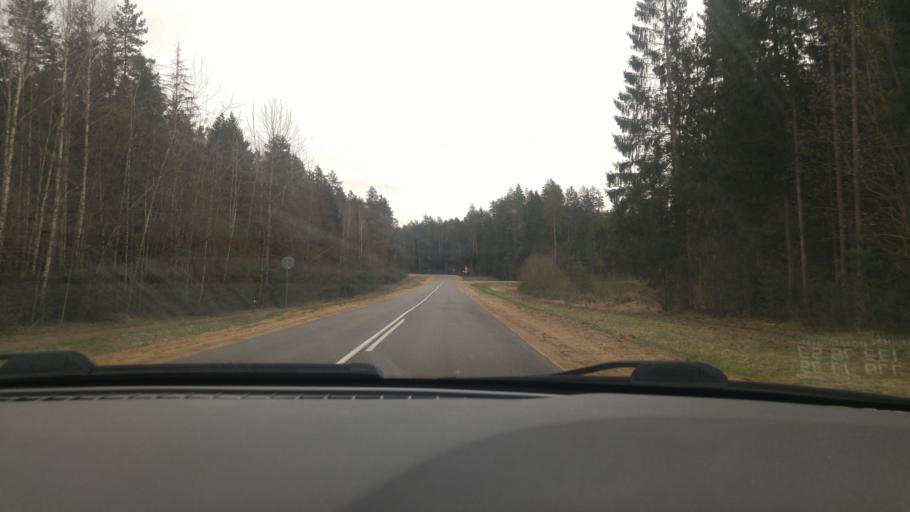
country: BY
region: Minsk
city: Chervyen'
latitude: 53.7348
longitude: 28.3022
